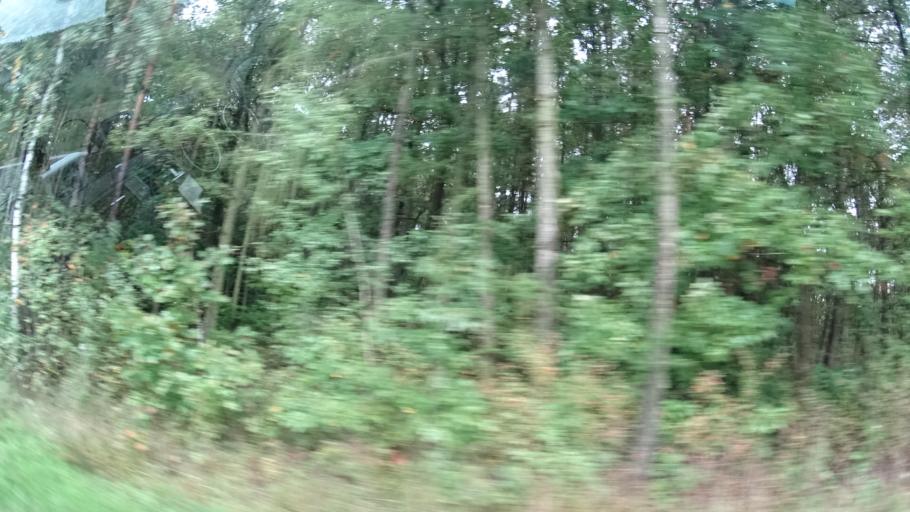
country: DE
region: Bavaria
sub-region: Upper Franconia
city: Breitengussbach
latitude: 49.9718
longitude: 10.9199
